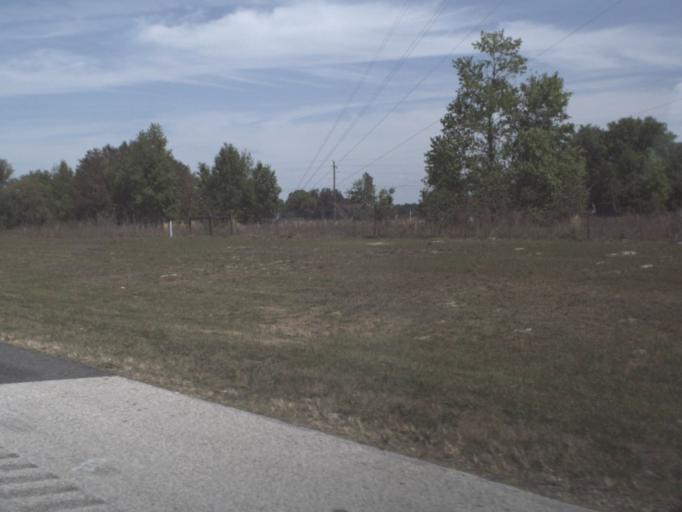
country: US
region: Florida
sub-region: Sumter County
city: Wildwood
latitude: 28.9333
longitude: -82.1119
